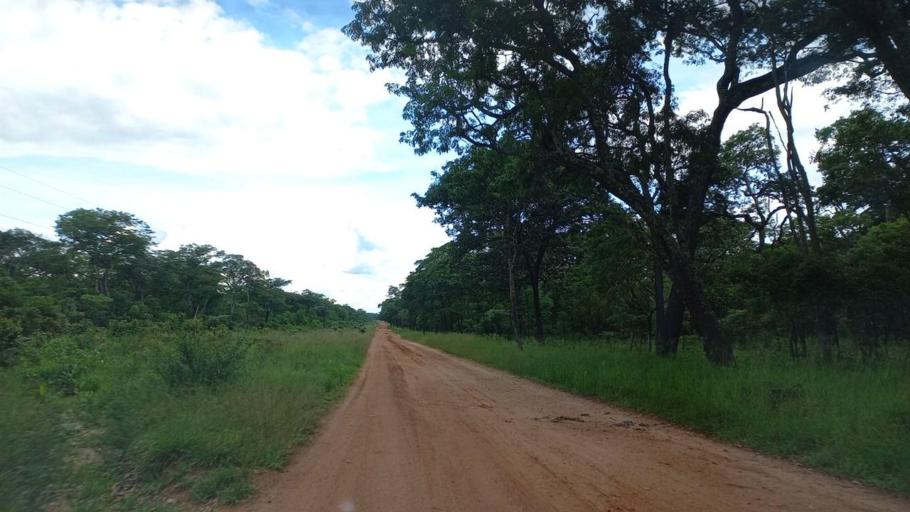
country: ZM
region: North-Western
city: Mwinilunga
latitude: -11.8045
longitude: 24.3693
